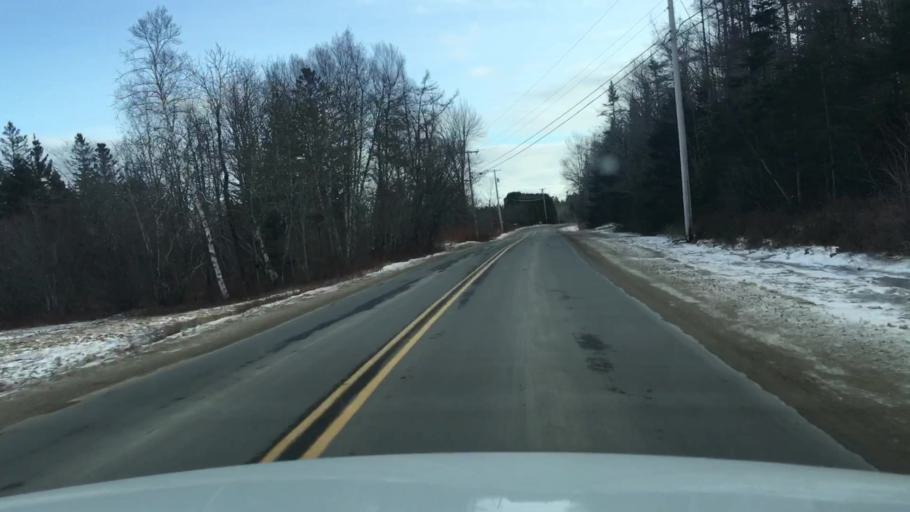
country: US
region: Maine
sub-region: Washington County
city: Jonesport
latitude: 44.6148
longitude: -67.6041
